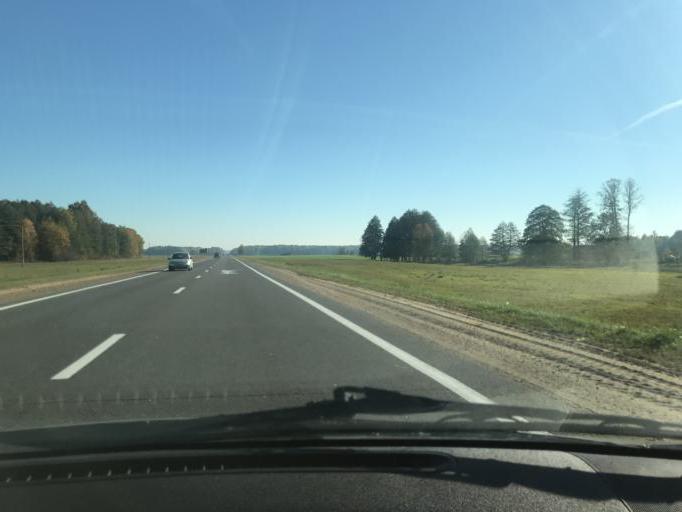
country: BY
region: Brest
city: Ivanava
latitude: 52.1561
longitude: 25.7028
